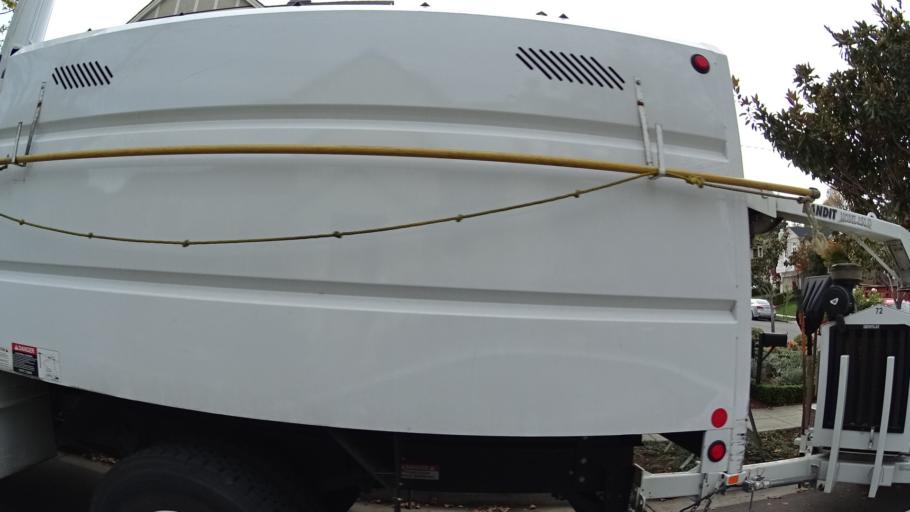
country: US
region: California
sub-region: San Mateo County
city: Hillsborough
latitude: 37.5816
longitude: -122.3797
